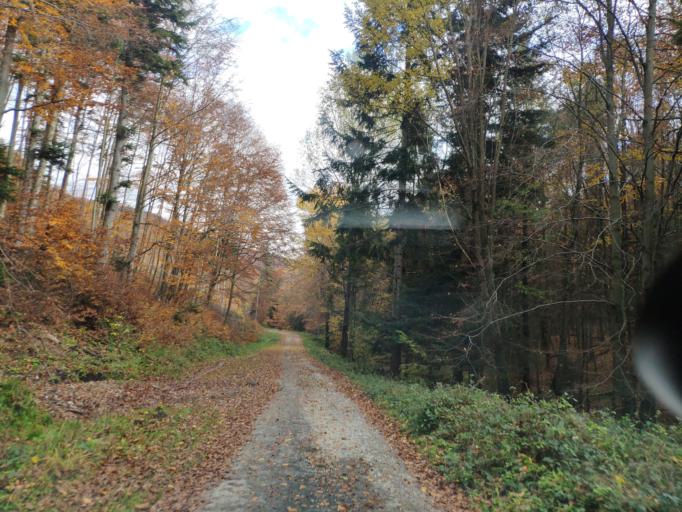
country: SK
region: Kosicky
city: Gelnica
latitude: 48.7614
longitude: 20.9764
